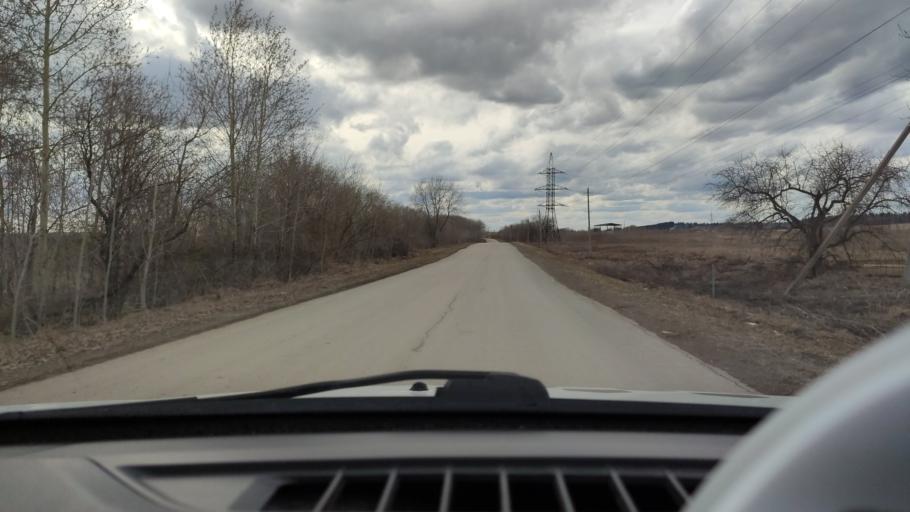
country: RU
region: Perm
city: Froly
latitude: 57.9297
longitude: 56.2516
